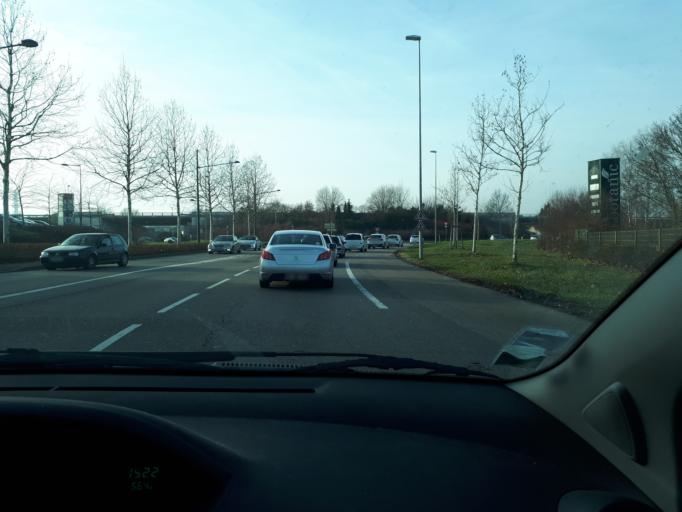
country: FR
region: Alsace
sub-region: Departement du Haut-Rhin
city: Didenheim
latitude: 47.7370
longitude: 7.2907
